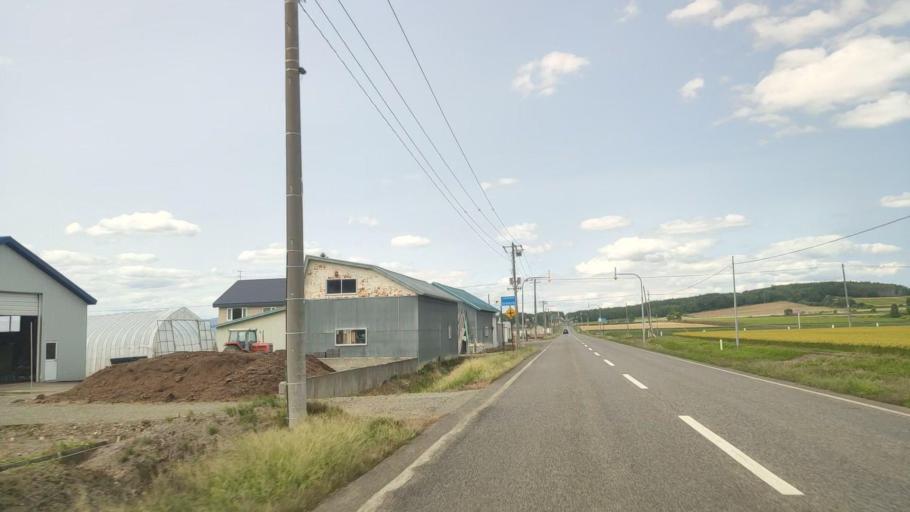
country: JP
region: Hokkaido
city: Nayoro
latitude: 44.2301
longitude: 142.4157
